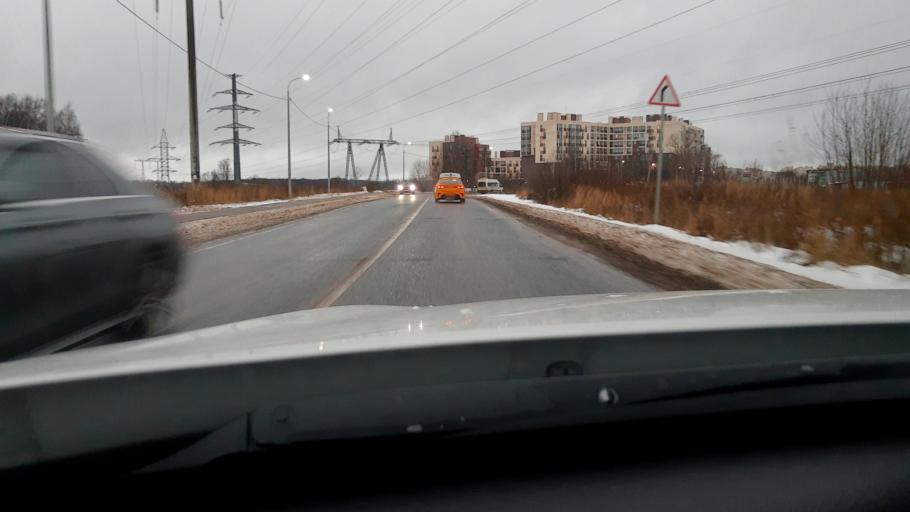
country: RU
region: Moskovskaya
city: Krasnogorsk
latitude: 55.8692
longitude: 37.3112
